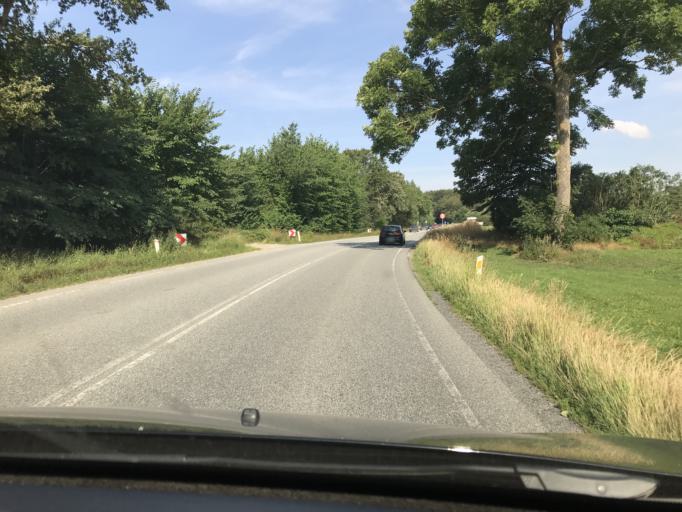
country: DK
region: Central Jutland
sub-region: Norddjurs Kommune
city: Allingabro
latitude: 56.4360
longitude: 10.3424
